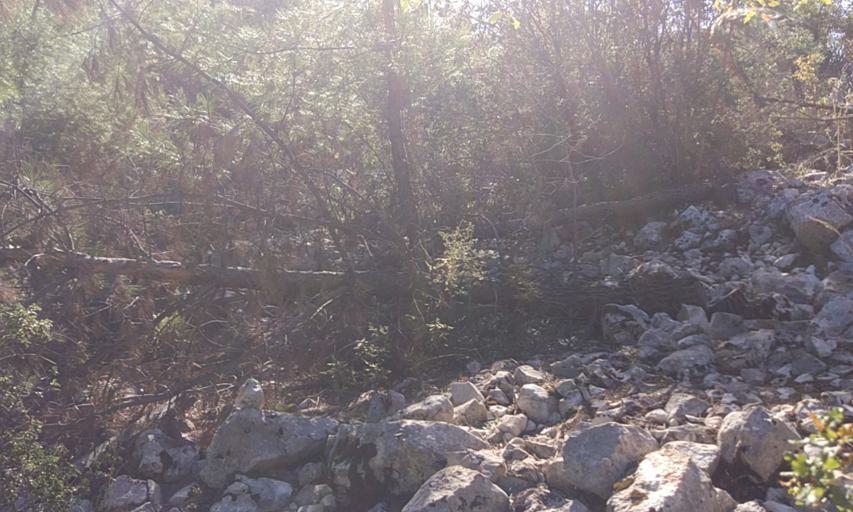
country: TR
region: Antalya
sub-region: Kemer
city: Goeynuek
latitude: 36.6340
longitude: 30.4471
